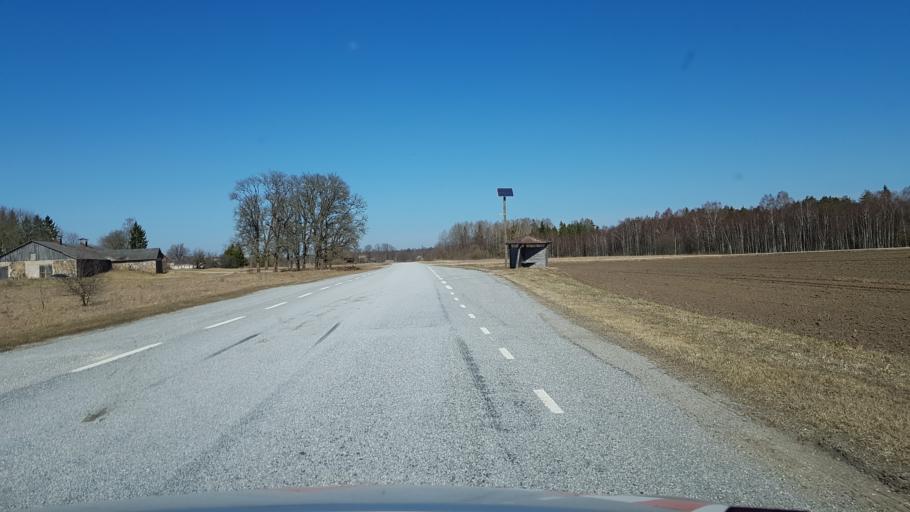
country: EE
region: Jaervamaa
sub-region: Koeru vald
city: Koeru
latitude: 59.0372
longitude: 26.0916
